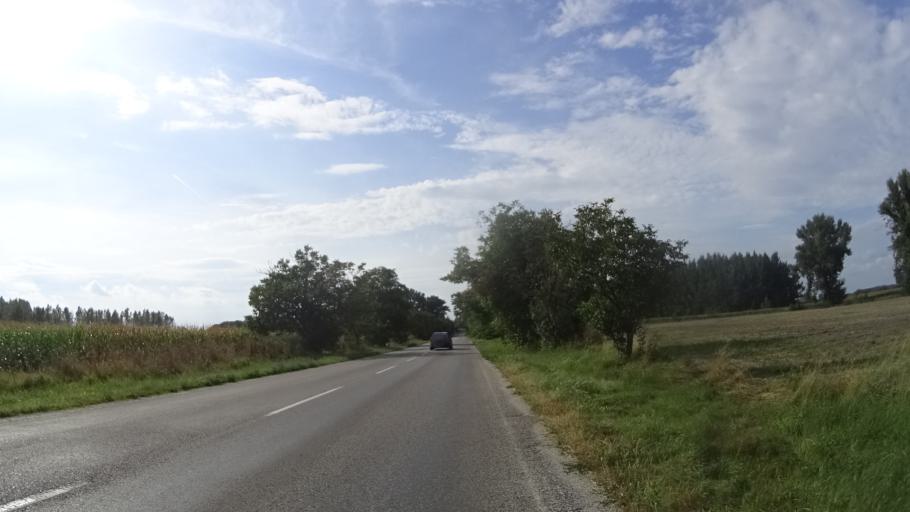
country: SK
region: Trnavsky
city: Gabcikovo
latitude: 47.9258
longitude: 17.4919
